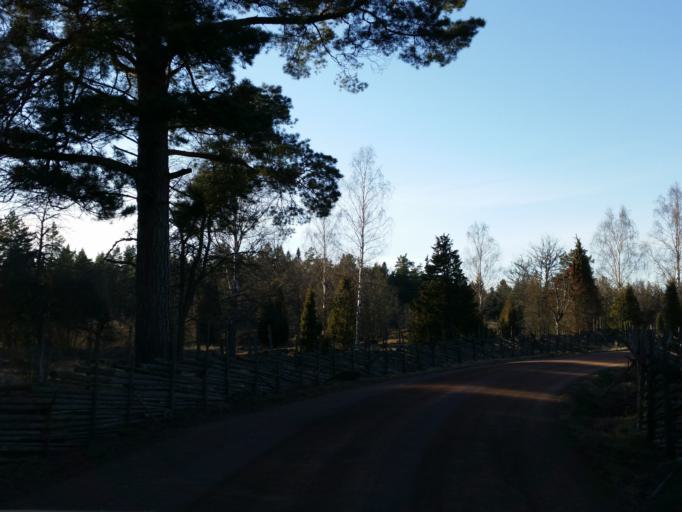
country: SE
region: Kalmar
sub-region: Oskarshamns Kommun
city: Oskarshamn
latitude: 57.3346
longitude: 16.4753
